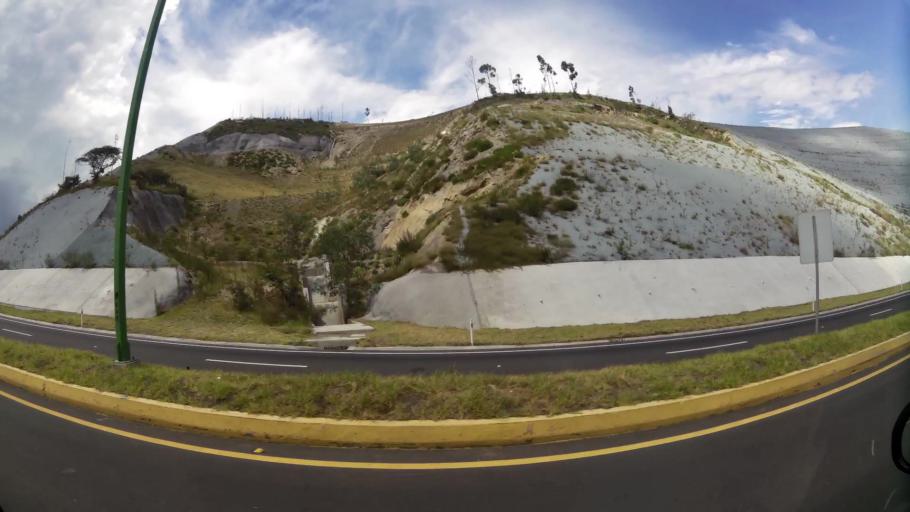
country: EC
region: Pichincha
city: Quito
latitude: -0.1014
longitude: -78.3743
